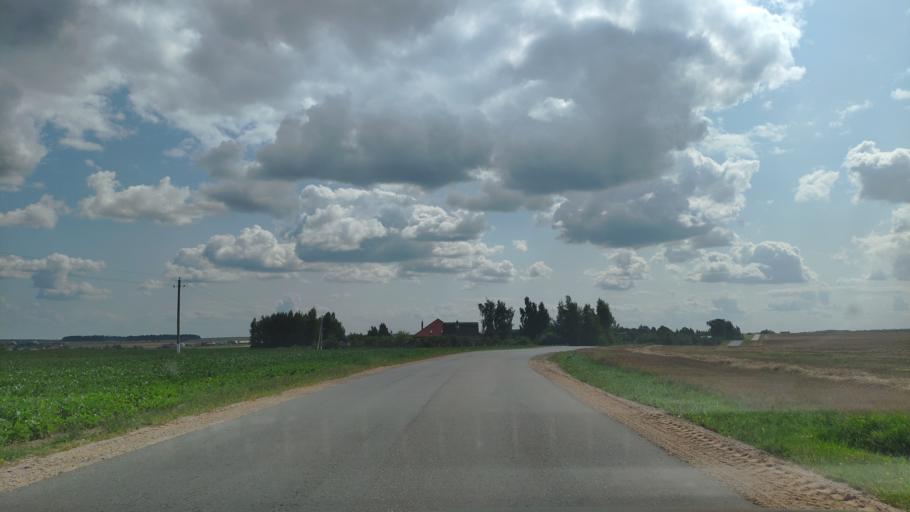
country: BY
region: Minsk
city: Khatsyezhyna
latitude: 53.8429
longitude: 27.3132
